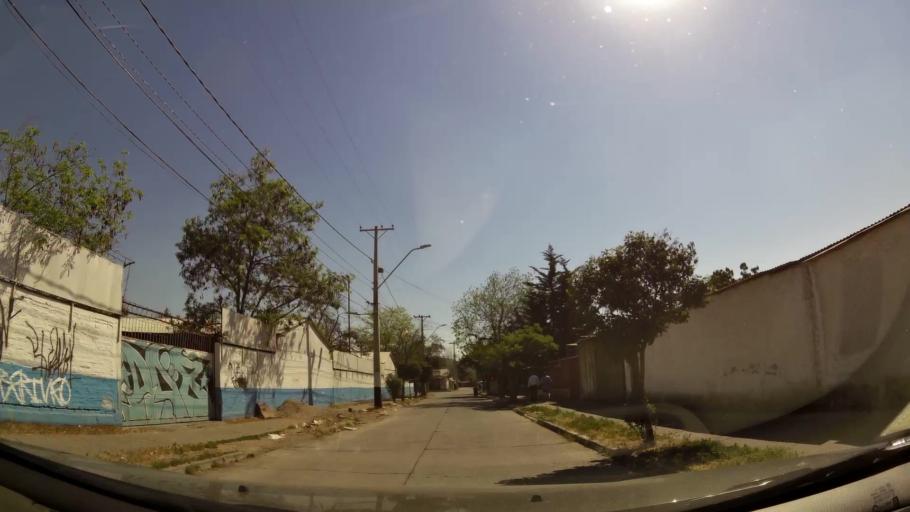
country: CL
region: Santiago Metropolitan
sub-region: Provincia de Maipo
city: San Bernardo
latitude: -33.5806
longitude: -70.7056
